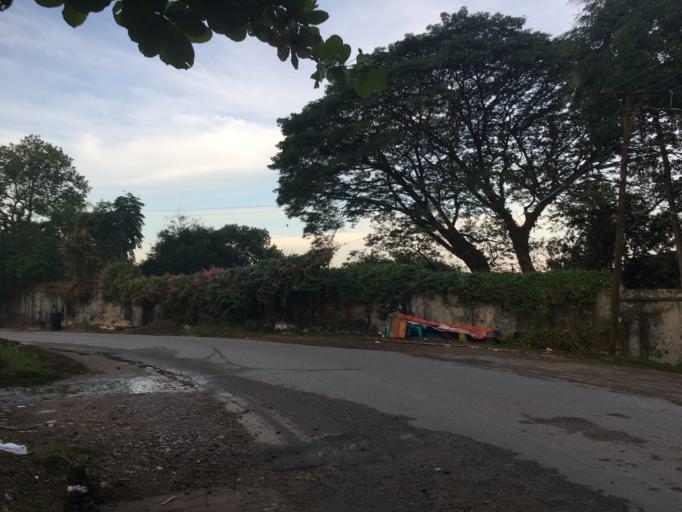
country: MM
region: Mon
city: Mawlamyine
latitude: 16.4867
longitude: 97.6267
